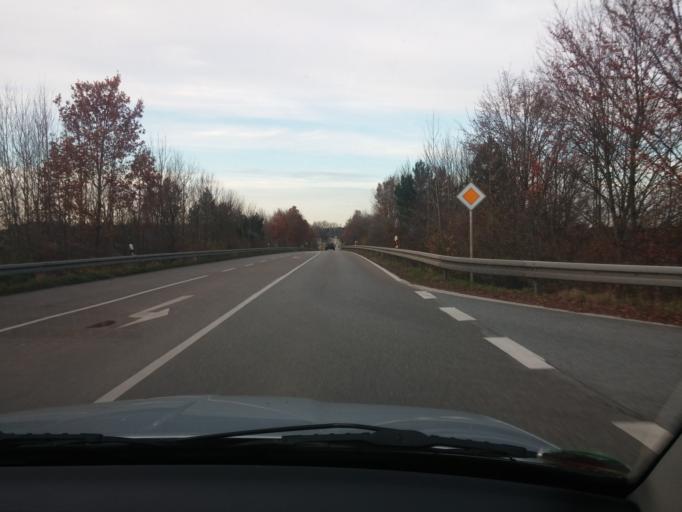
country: DE
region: Bavaria
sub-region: Upper Bavaria
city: Forstinning
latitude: 48.1709
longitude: 11.8898
